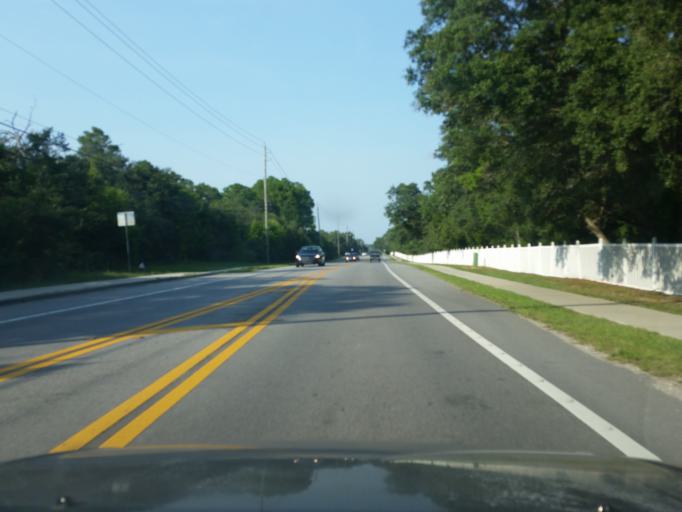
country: US
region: Florida
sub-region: Escambia County
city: Warrington
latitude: 30.3316
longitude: -87.3549
